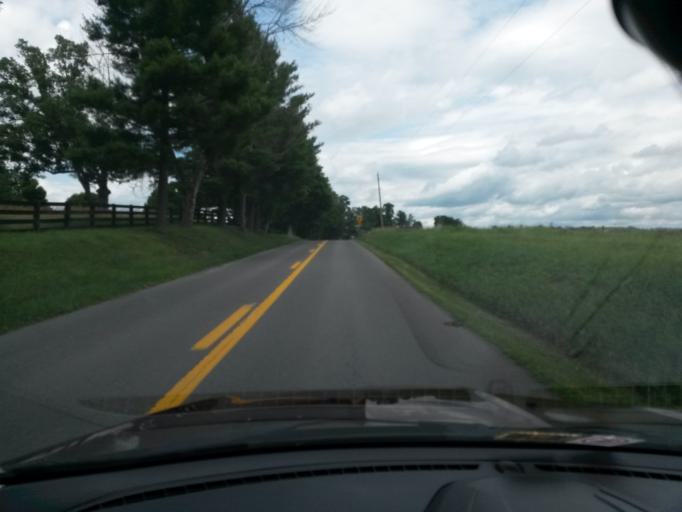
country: US
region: West Virginia
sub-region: Monroe County
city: Union
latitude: 37.5468
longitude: -80.5326
